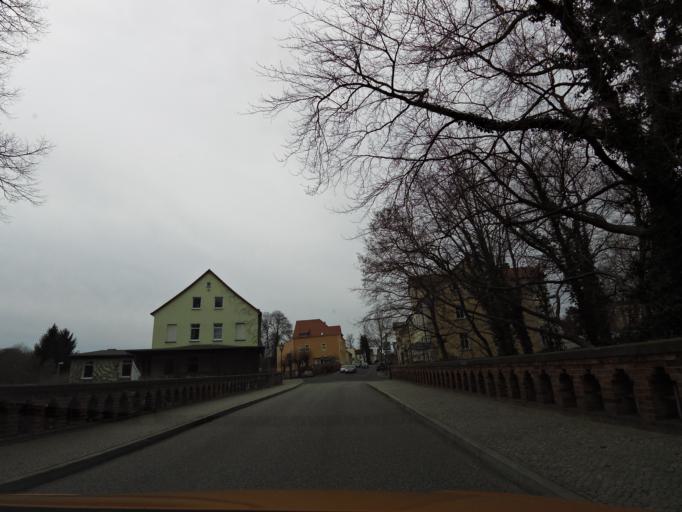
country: DE
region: Brandenburg
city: Belzig
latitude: 52.1411
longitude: 12.5847
